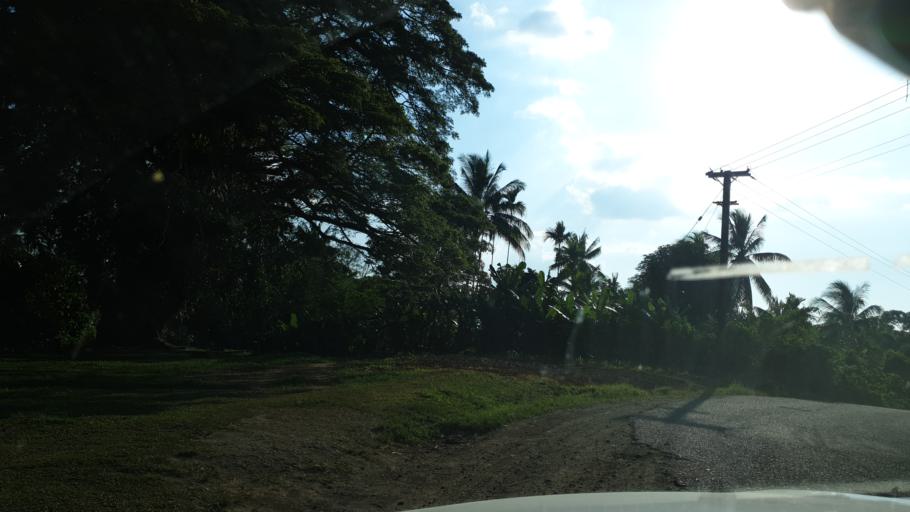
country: PG
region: East Sepik
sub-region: Wewak
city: Wewak
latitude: -3.7043
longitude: 143.6405
